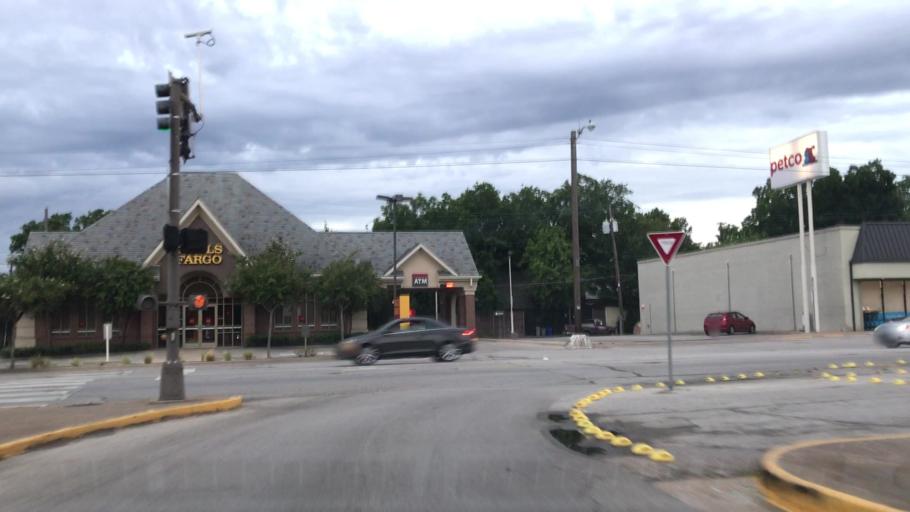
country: US
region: Texas
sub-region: Dallas County
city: University Park
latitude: 32.8514
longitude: -96.8087
